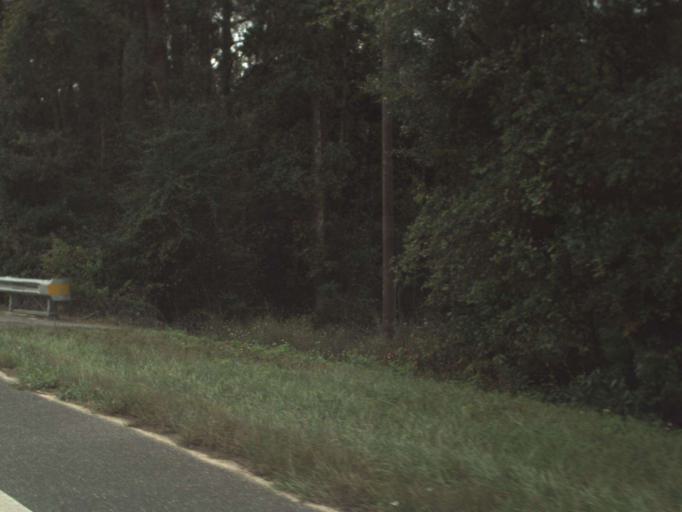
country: US
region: Florida
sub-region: Calhoun County
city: Blountstown
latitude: 30.4460
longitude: -85.1829
